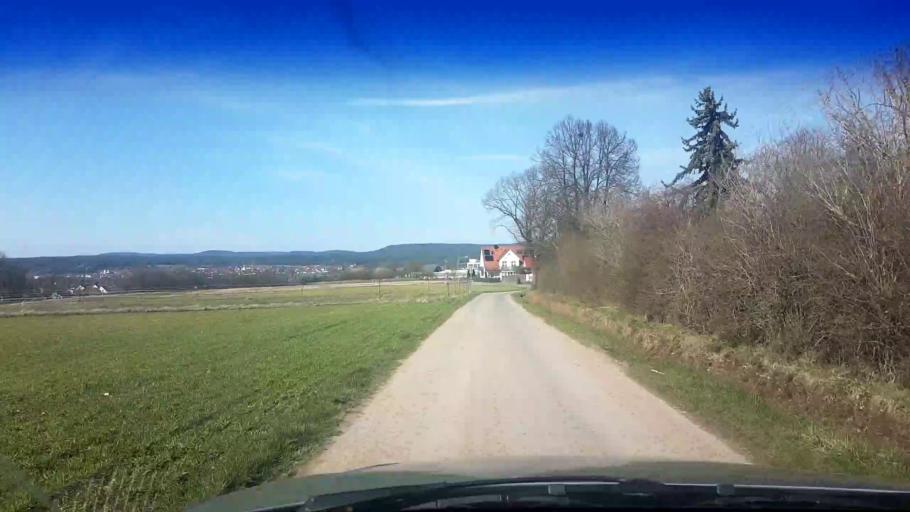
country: DE
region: Bavaria
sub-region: Upper Franconia
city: Bischberg
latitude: 49.9051
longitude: 10.8258
